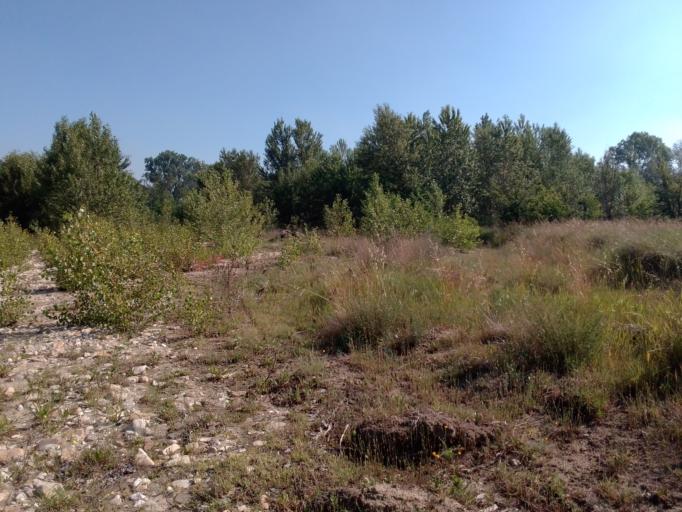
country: IT
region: Emilia-Romagna
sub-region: Provincia di Piacenza
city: Borgonovo Valtidone
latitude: 44.9952
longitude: 9.4855
